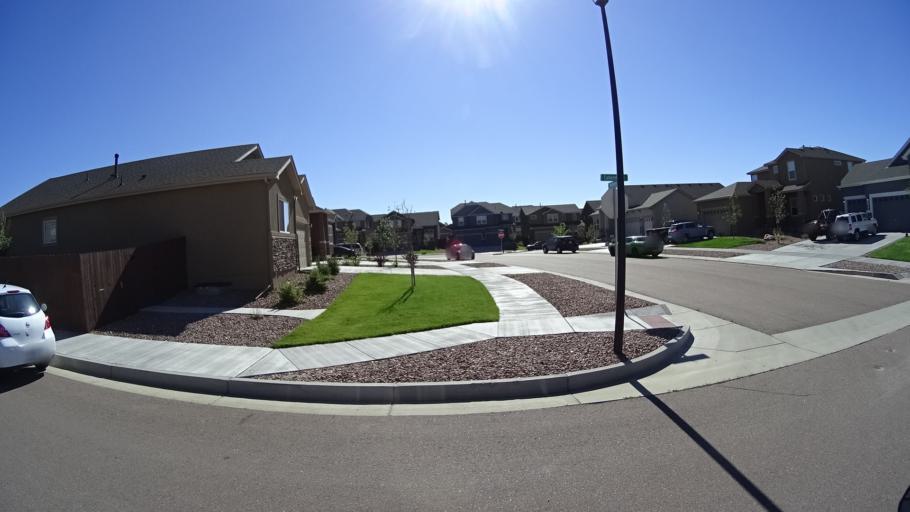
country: US
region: Colorado
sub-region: El Paso County
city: Black Forest
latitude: 38.9493
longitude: -104.6755
